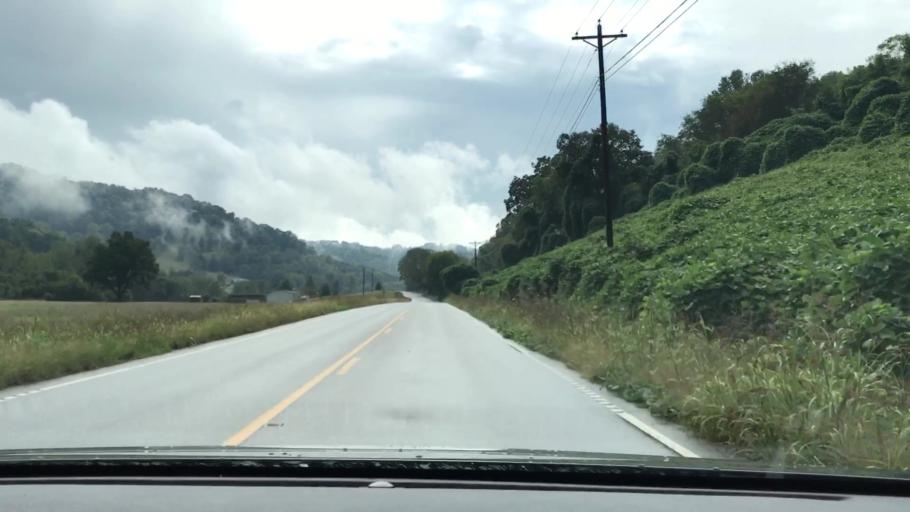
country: US
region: Tennessee
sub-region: Smith County
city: Carthage
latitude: 36.3759
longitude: -85.9501
